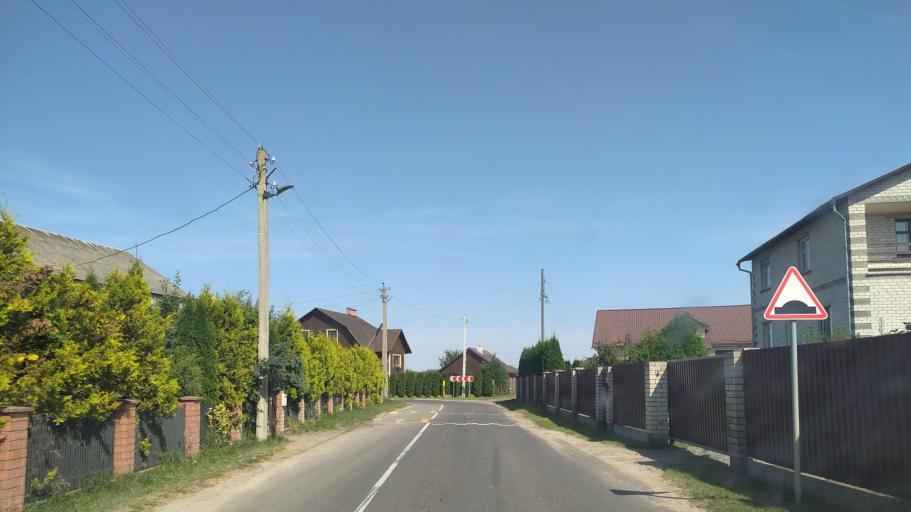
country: BY
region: Brest
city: Byaroza
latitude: 52.5294
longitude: 24.9948
